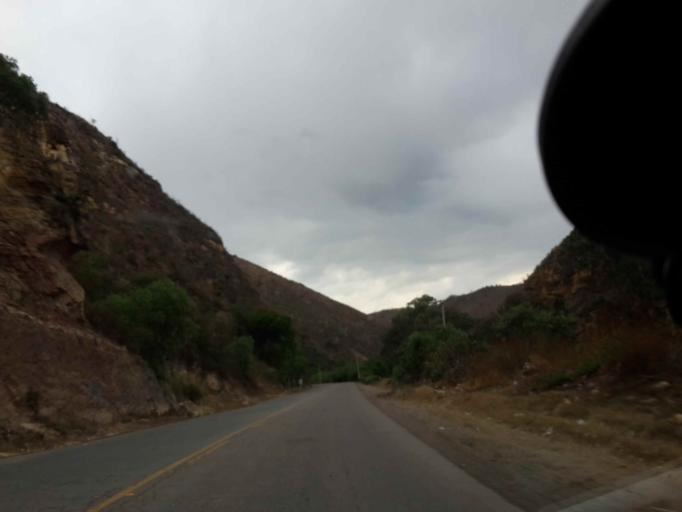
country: BO
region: Cochabamba
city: Sipe Sipe
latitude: -17.5303
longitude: -66.3360
